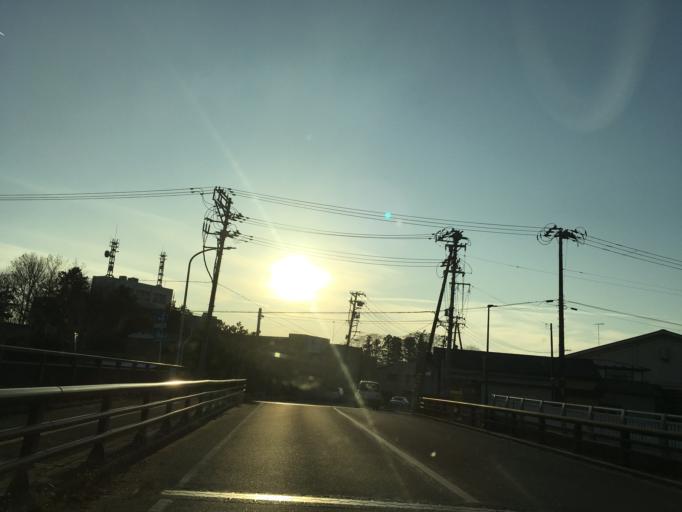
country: JP
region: Miyagi
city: Wakuya
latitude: 38.6851
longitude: 141.1996
